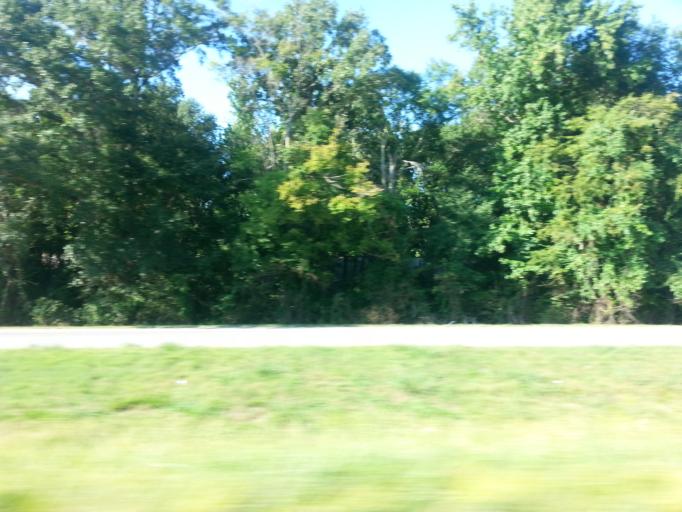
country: US
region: Alabama
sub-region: Colbert County
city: Tuscumbia
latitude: 34.7188
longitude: -87.7972
